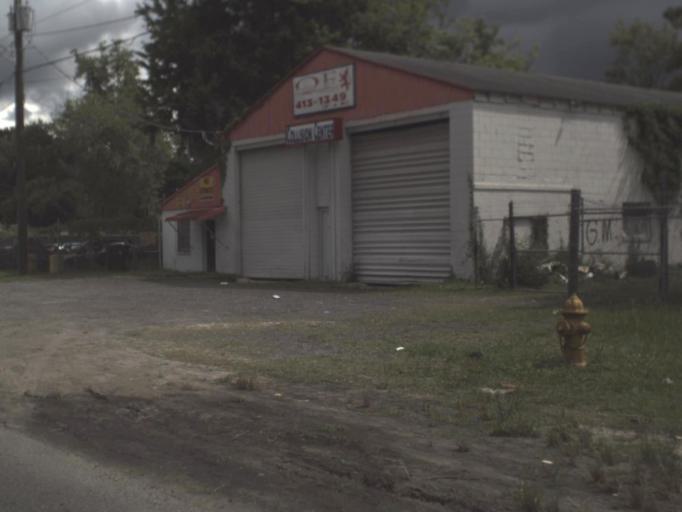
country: US
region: Florida
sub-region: Duval County
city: Jacksonville
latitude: 30.4020
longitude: -81.7417
